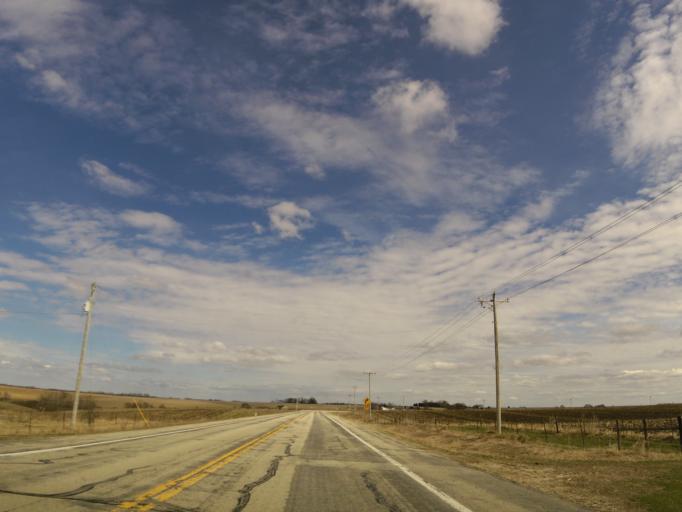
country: US
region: Minnesota
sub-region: Olmsted County
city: Rochester
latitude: 43.9459
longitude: -92.4139
